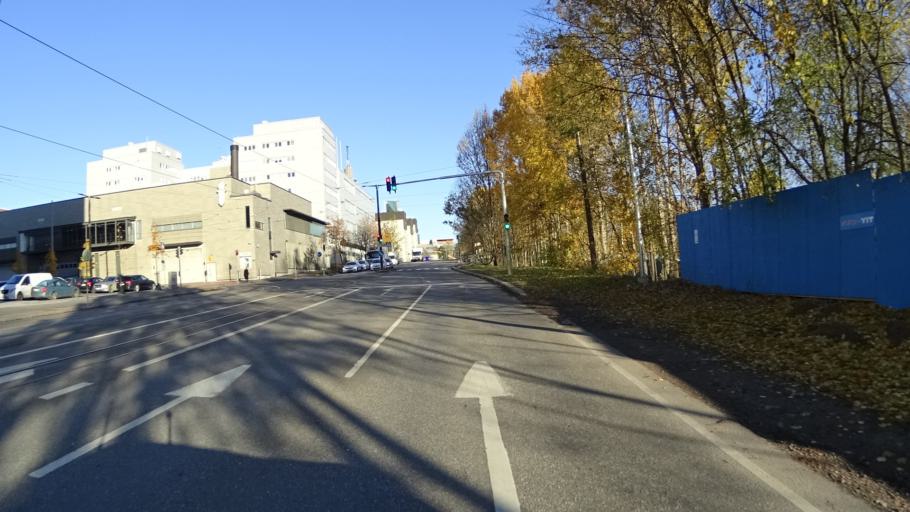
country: FI
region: Uusimaa
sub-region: Helsinki
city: Helsinki
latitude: 60.1999
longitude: 24.9273
